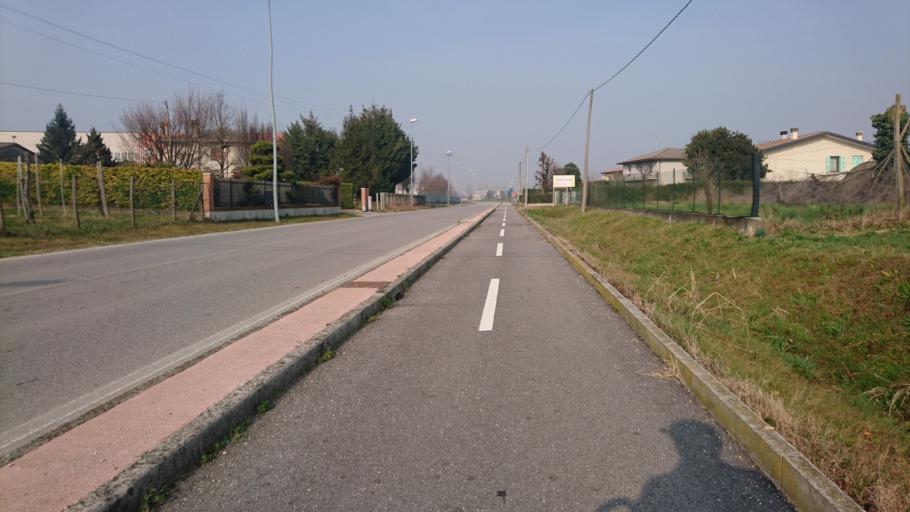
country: IT
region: Veneto
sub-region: Provincia di Padova
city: Veggiano
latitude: 45.4551
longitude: 11.7004
